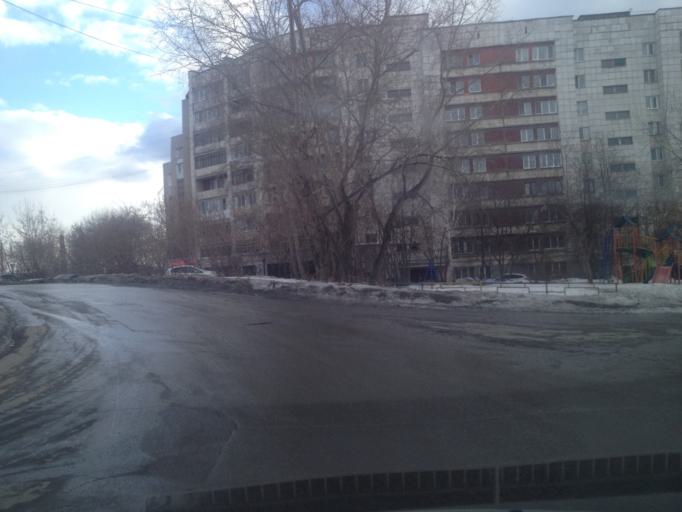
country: RU
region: Sverdlovsk
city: Yekaterinburg
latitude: 56.8552
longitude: 60.5820
